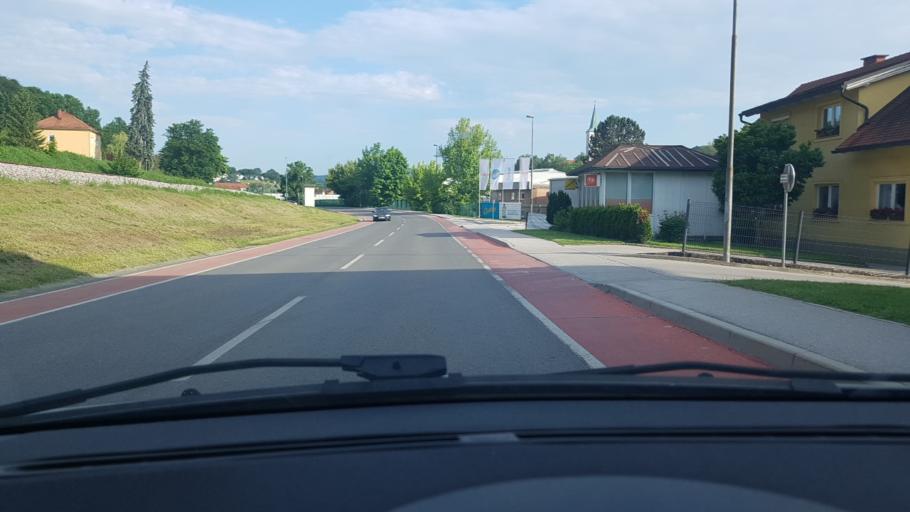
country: SI
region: Rogaska Slatina
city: Rogaska Slatina
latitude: 46.2290
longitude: 15.6385
